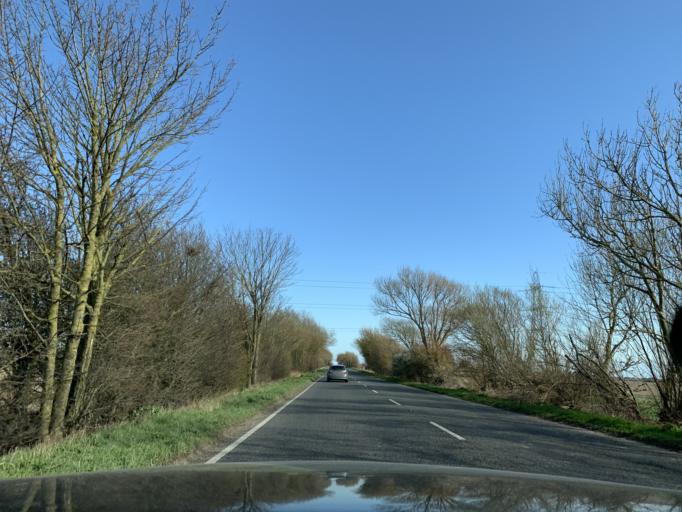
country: GB
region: England
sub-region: Kent
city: New Romney
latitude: 50.9871
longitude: 0.9098
